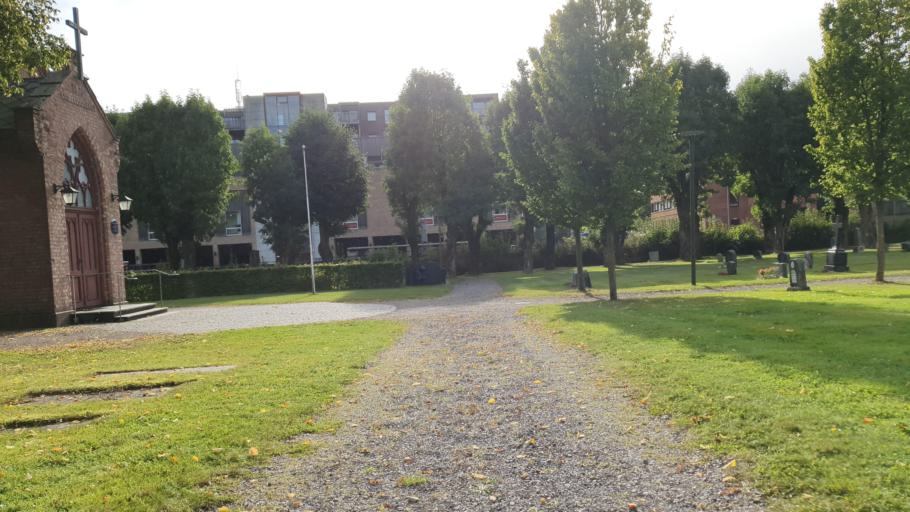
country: NO
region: Vestfold
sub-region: Tonsberg
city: Tonsberg
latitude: 59.2706
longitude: 10.4132
